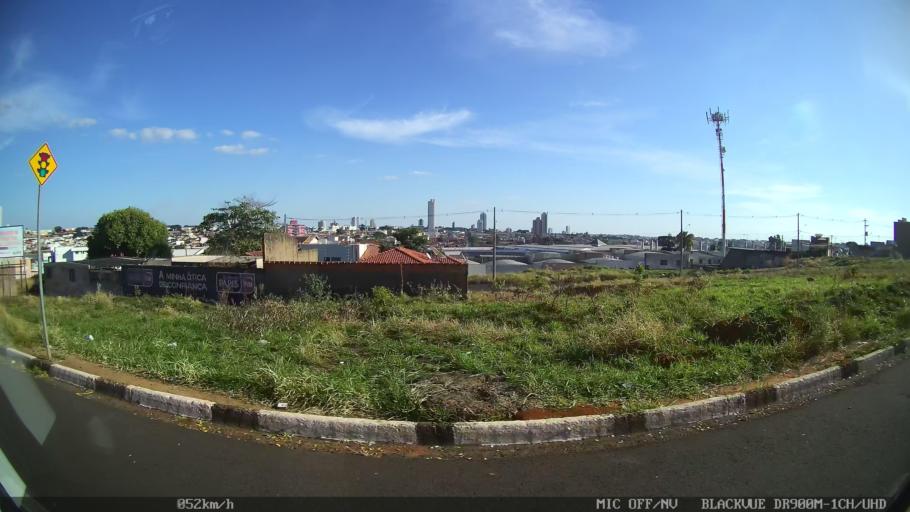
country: BR
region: Sao Paulo
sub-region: Franca
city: Franca
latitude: -20.5174
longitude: -47.3834
